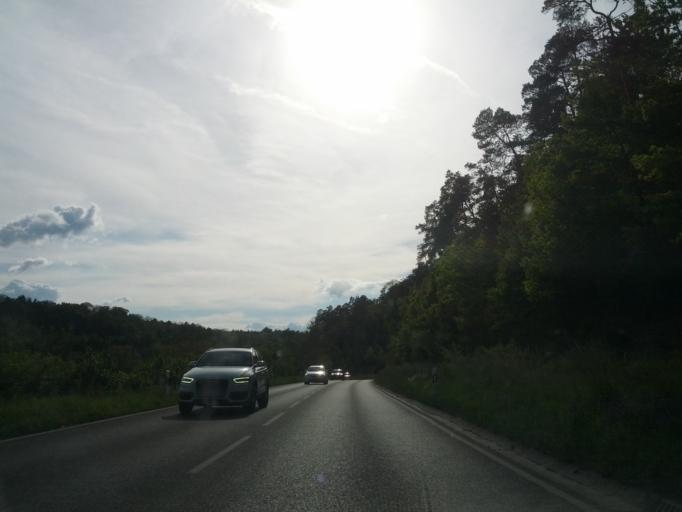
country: DE
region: Baden-Wuerttemberg
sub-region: Regierungsbezirk Stuttgart
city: Aidlingen
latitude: 48.6996
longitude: 8.9305
